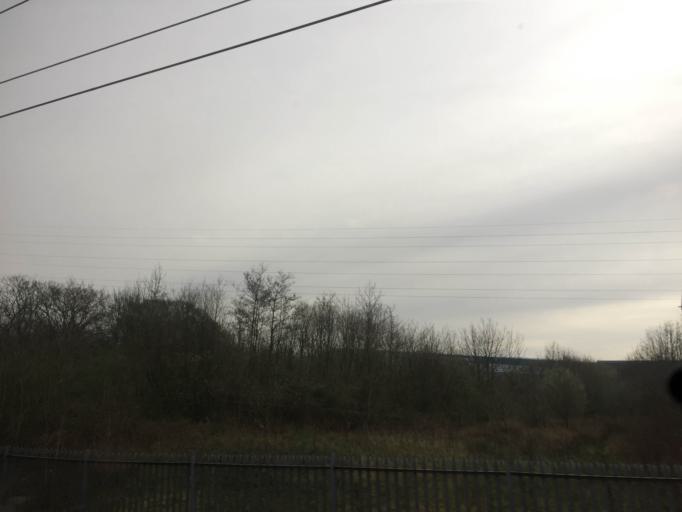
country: GB
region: England
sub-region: Borough of Wigan
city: Golborne
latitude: 53.4706
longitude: -2.5961
